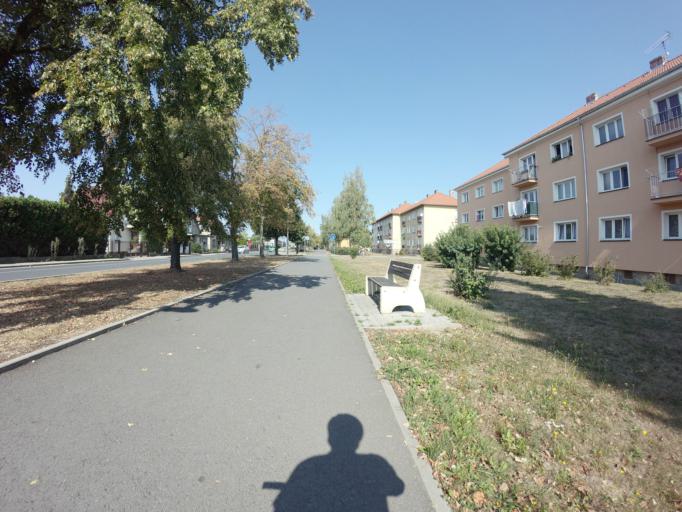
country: CZ
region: Central Bohemia
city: Tynec nad Sazavou
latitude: 49.8362
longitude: 14.5850
